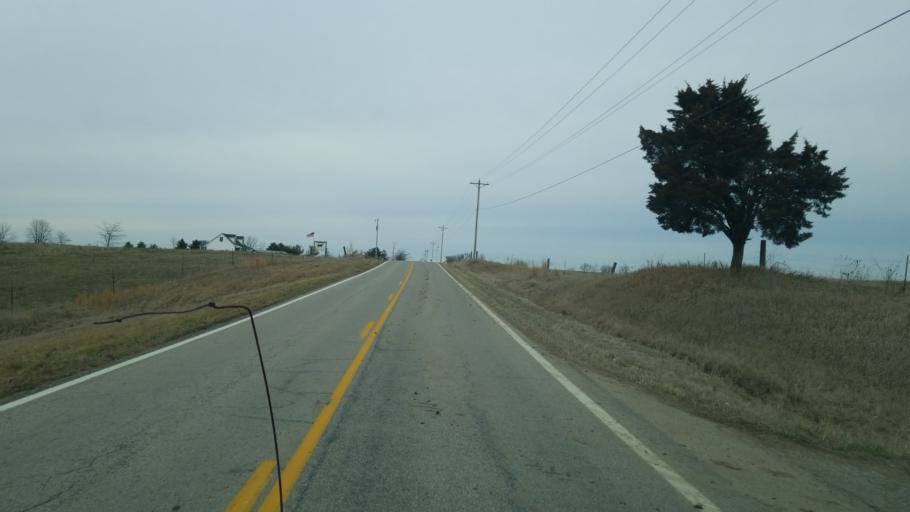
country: US
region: Ohio
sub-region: Pickaway County
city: Williamsport
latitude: 39.5403
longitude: -83.1228
